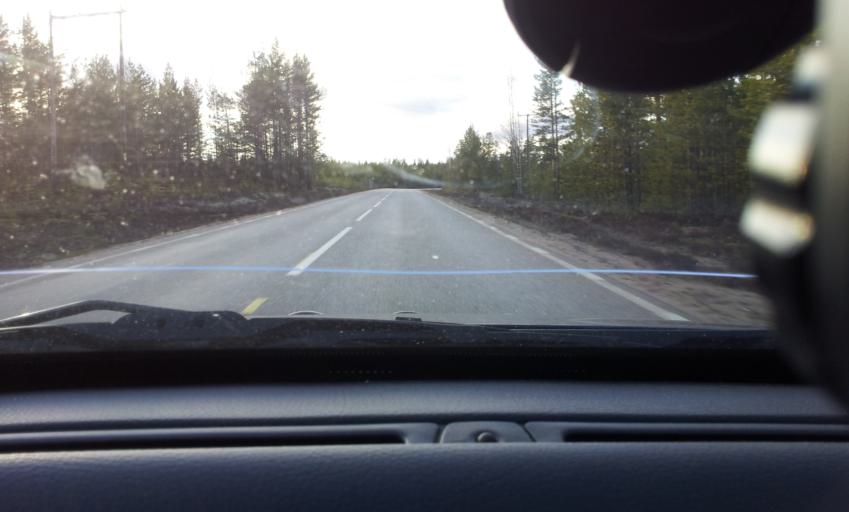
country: SE
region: Jaemtland
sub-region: Harjedalens Kommun
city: Sveg
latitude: 62.1152
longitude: 15.0487
